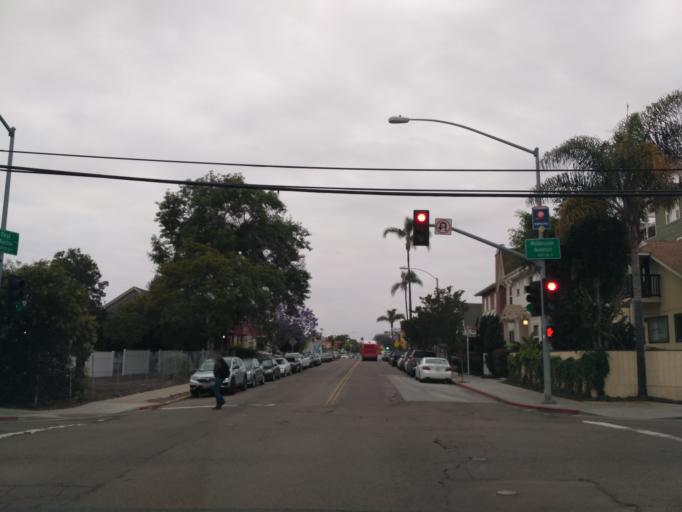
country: US
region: California
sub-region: San Diego County
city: San Diego
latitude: 32.7467
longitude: -117.1639
